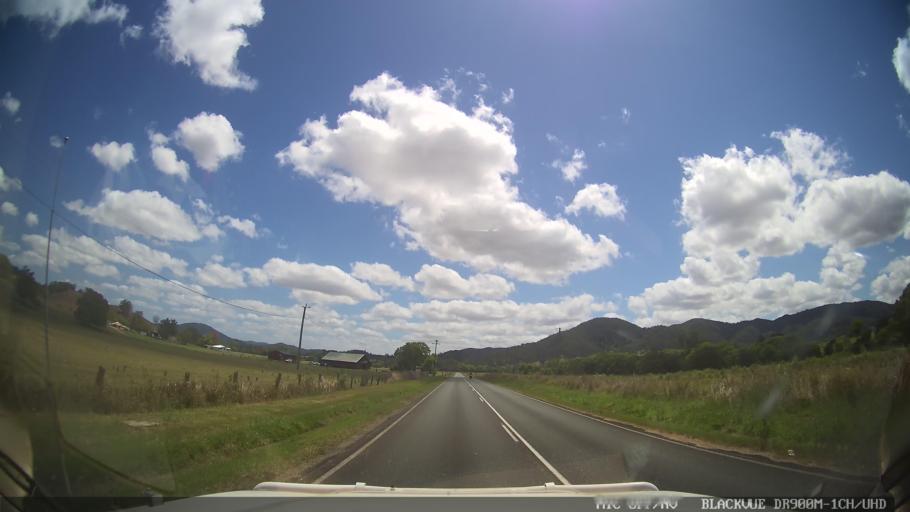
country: AU
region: Queensland
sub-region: Sunshine Coast
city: Nambour
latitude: -26.6492
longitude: 152.8114
